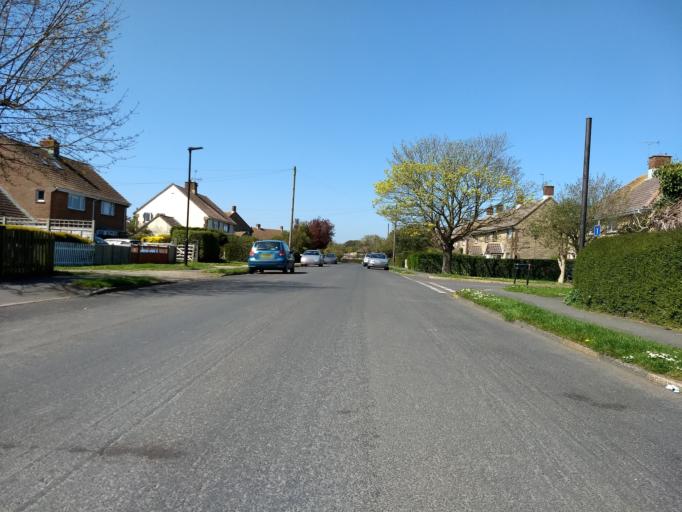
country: GB
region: England
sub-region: Isle of Wight
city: Bembridge
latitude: 50.6850
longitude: -1.0776
